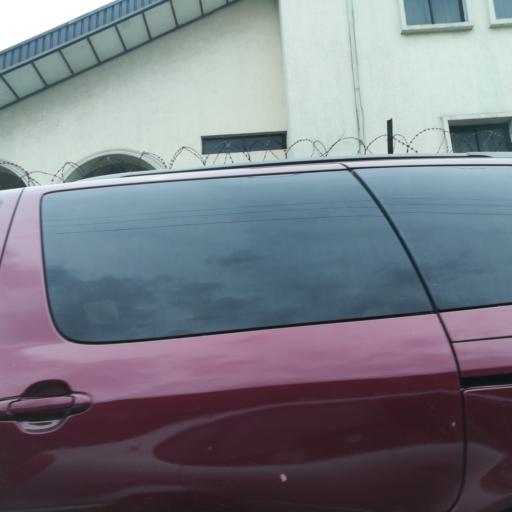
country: NG
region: Rivers
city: Port Harcourt
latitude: 4.8335
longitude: 7.0336
